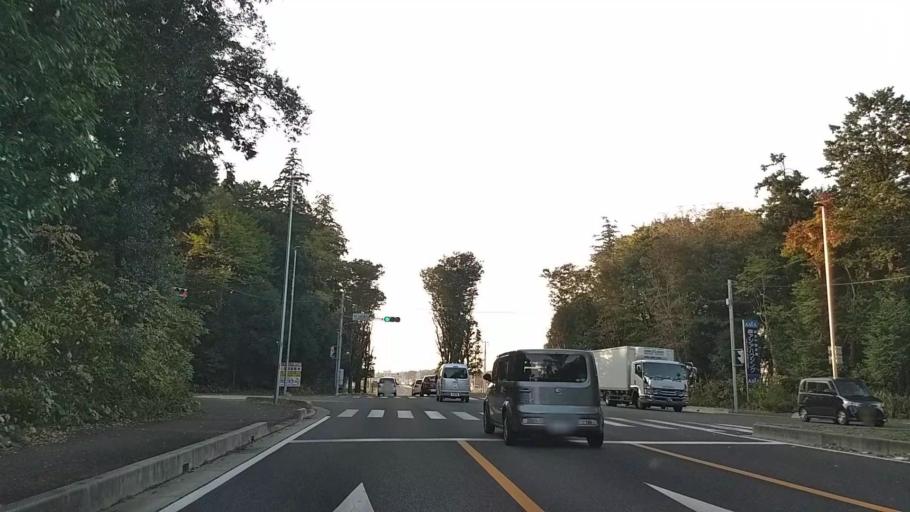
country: JP
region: Saitama
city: Sayama
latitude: 35.8438
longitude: 139.4521
